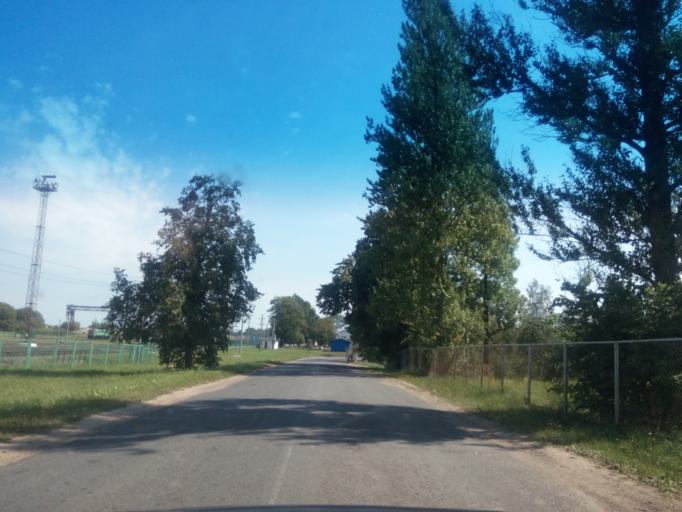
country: BY
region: Vitebsk
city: Vyerkhnyadzvinsk
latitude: 55.8349
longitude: 27.7333
